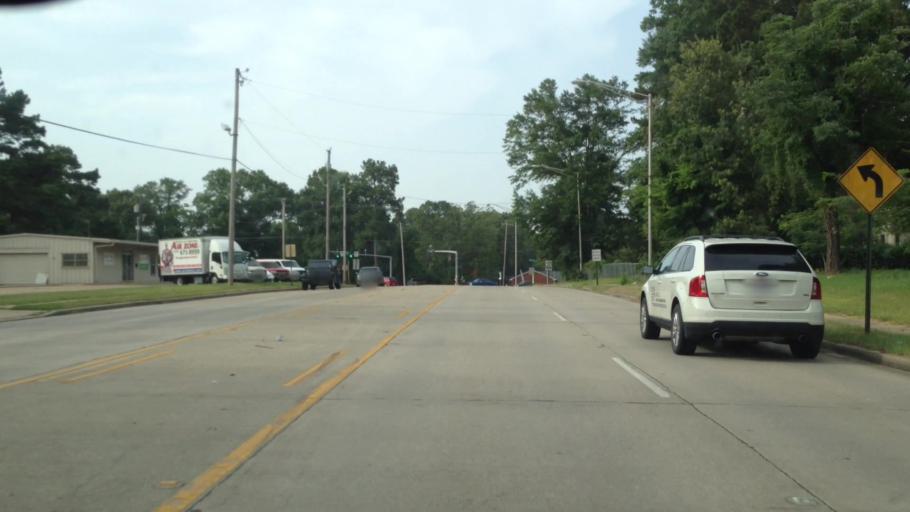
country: US
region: Louisiana
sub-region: De Soto Parish
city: Stonewall
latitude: 32.3960
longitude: -93.8147
